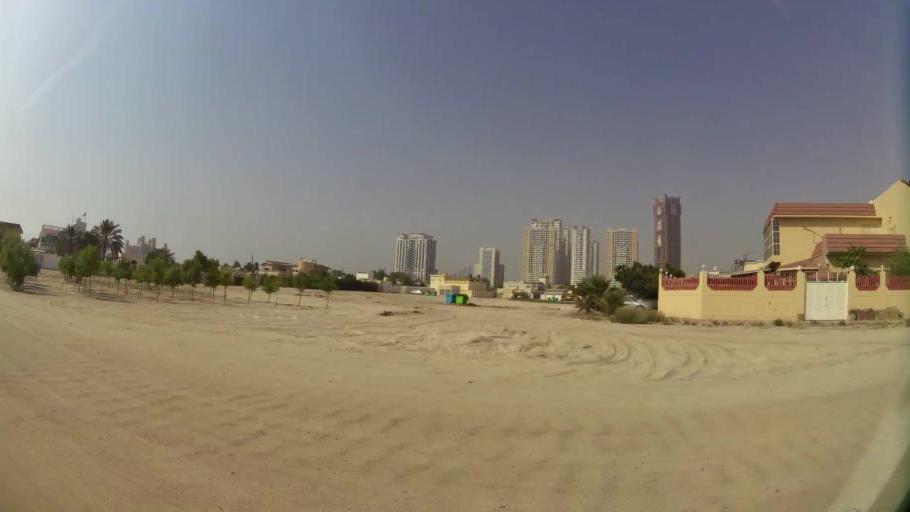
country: AE
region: Ajman
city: Ajman
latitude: 25.3889
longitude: 55.4258
